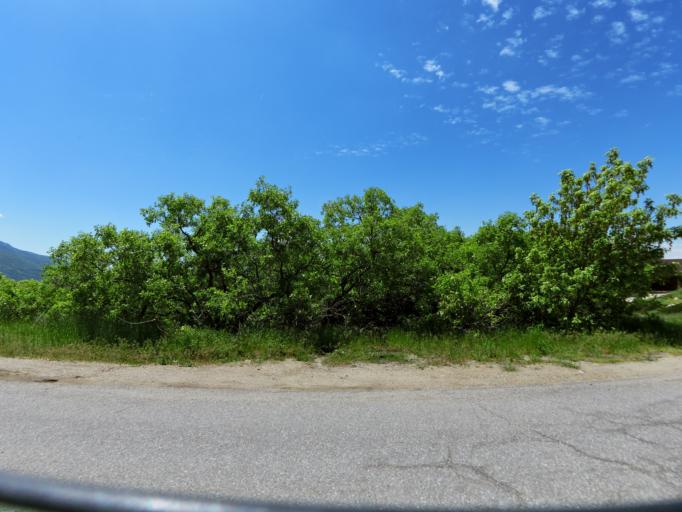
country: US
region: Utah
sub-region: Weber County
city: Uintah
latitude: 41.1638
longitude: -111.9192
